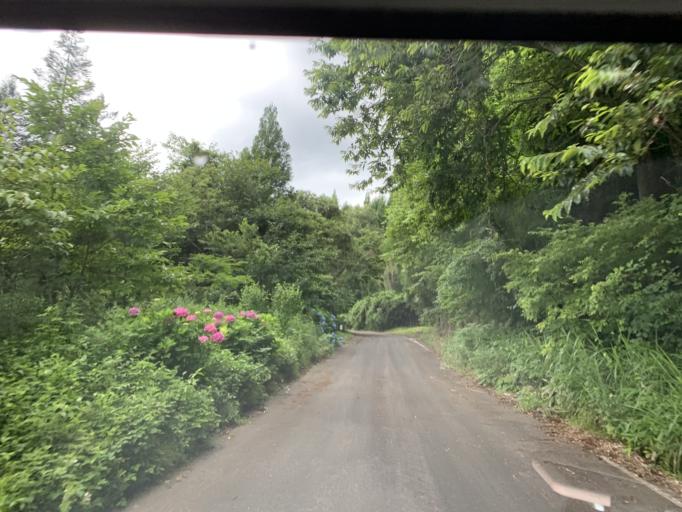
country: JP
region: Iwate
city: Ichinoseki
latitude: 38.9543
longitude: 141.0480
